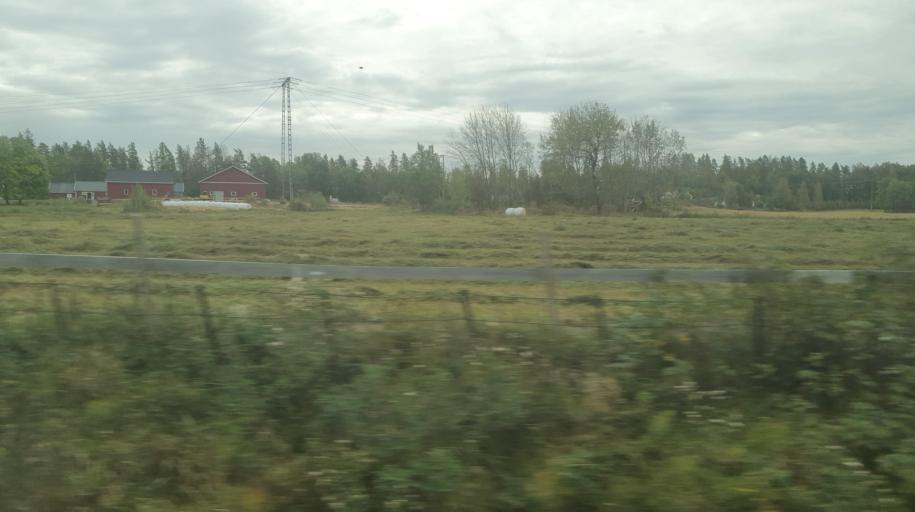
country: NO
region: Vestfold
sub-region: Horten
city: Skoppum
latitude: 59.3751
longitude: 10.4084
